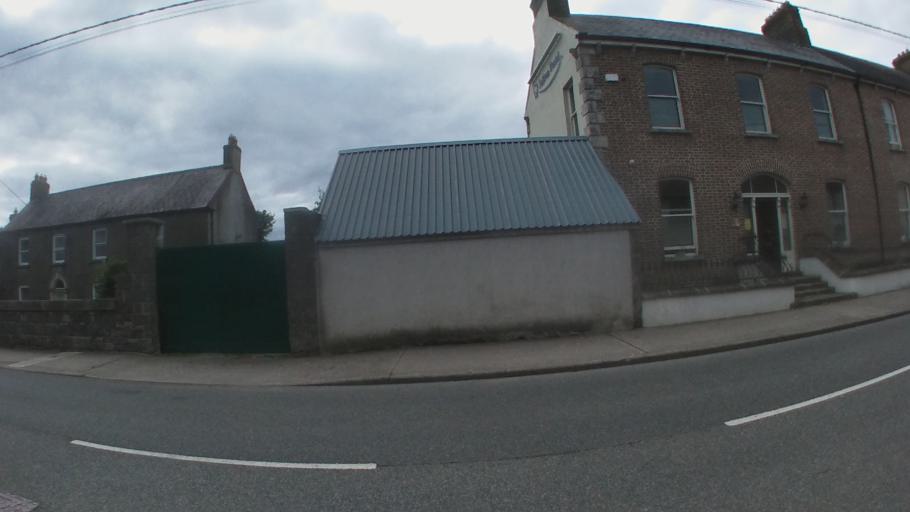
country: IE
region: Leinster
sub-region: County Carlow
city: Carlow
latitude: 52.8406
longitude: -6.9300
